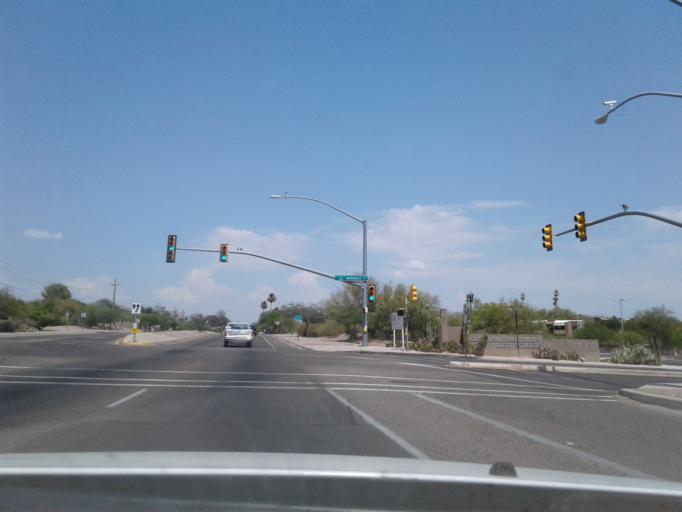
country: US
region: Arizona
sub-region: Pima County
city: Catalina Foothills
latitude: 32.3082
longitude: -110.8988
